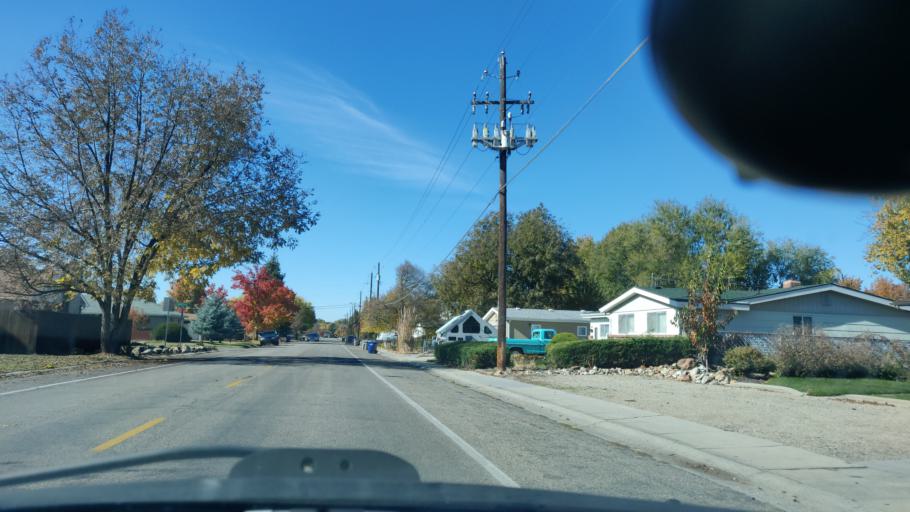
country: US
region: Idaho
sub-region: Ada County
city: Garden City
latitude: 43.5934
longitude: -116.2372
